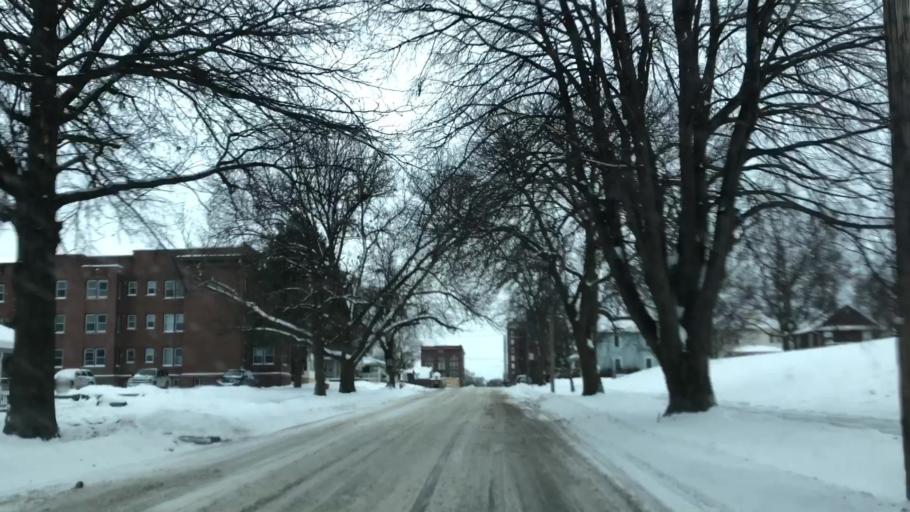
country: US
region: Iowa
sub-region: Marshall County
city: Marshalltown
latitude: 42.0524
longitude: -92.9097
